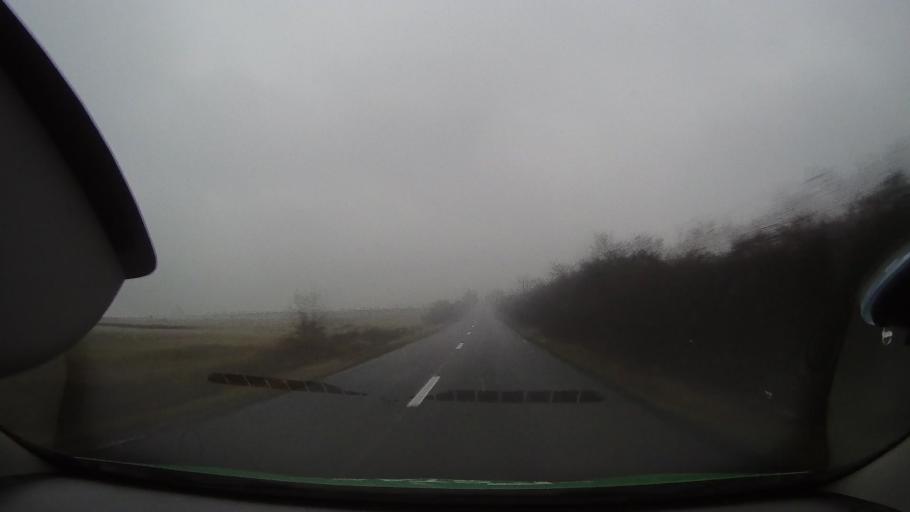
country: RO
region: Bihor
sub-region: Comuna Tinca
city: Gurbediu
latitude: 46.7733
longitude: 21.8894
